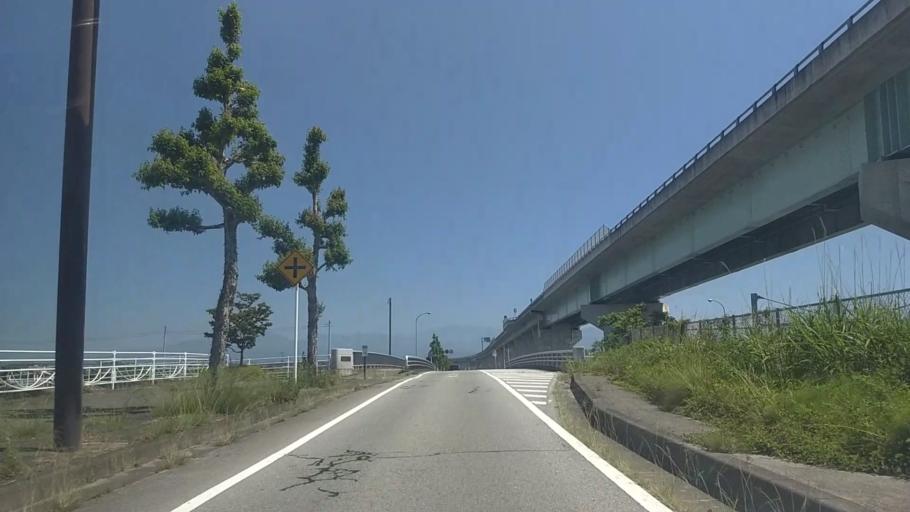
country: JP
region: Yamanashi
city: Ryuo
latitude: 35.6007
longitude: 138.4786
